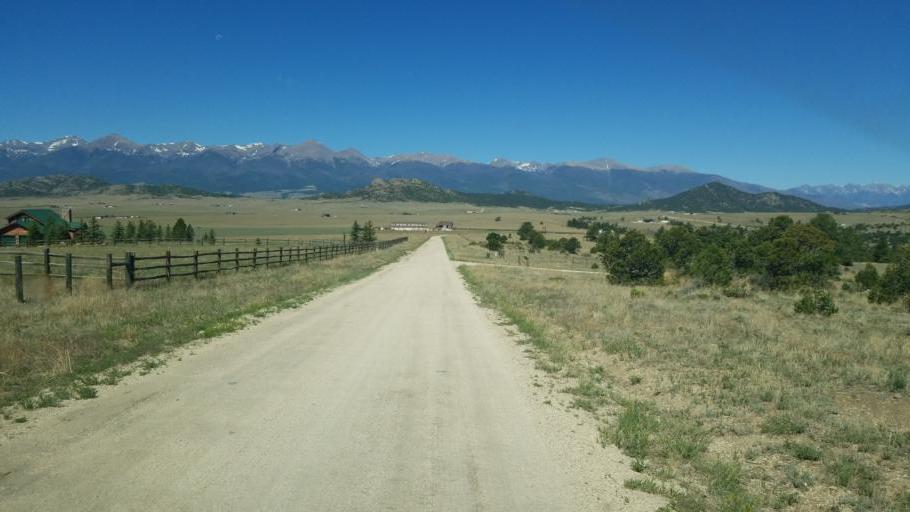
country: US
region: Colorado
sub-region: Custer County
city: Westcliffe
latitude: 38.2332
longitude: -105.4651
